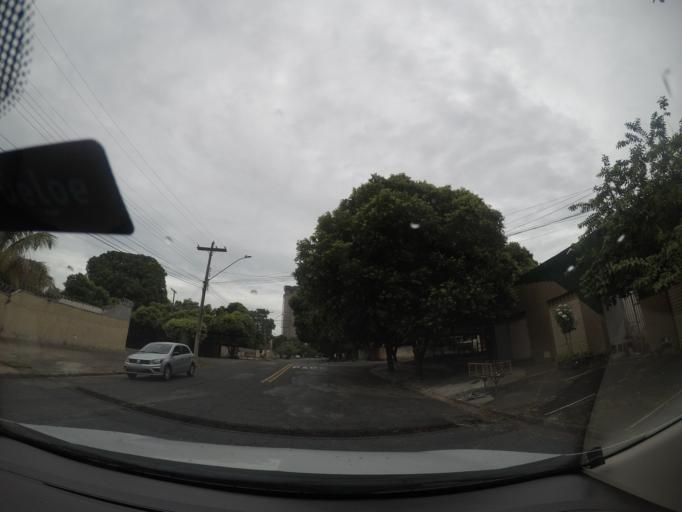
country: BR
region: Goias
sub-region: Goiania
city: Goiania
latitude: -16.6821
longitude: -49.2460
